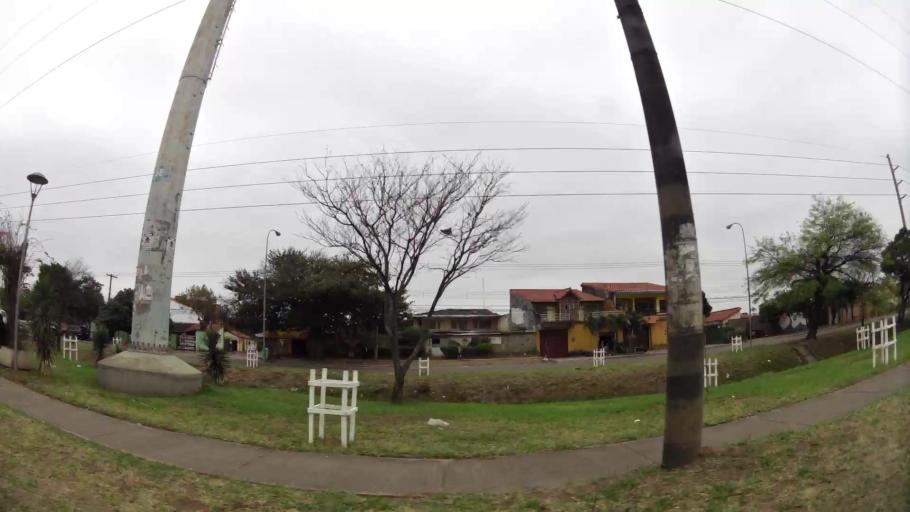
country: BO
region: Santa Cruz
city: Santa Cruz de la Sierra
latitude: -17.7672
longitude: -63.1478
